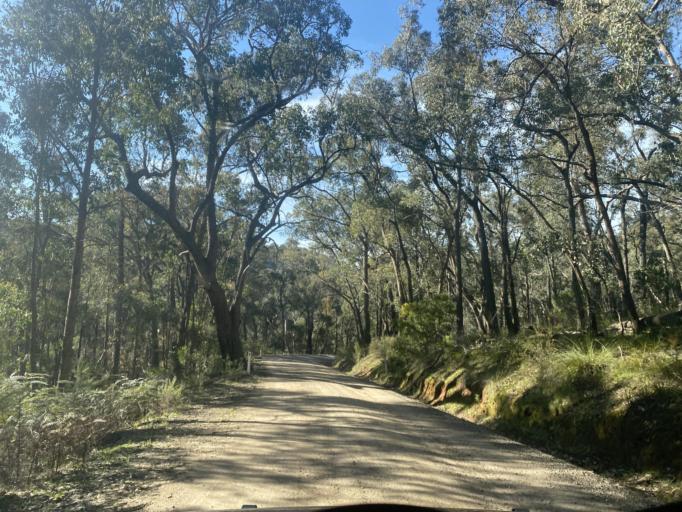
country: AU
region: Victoria
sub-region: Mansfield
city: Mansfield
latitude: -36.8257
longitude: 146.1526
